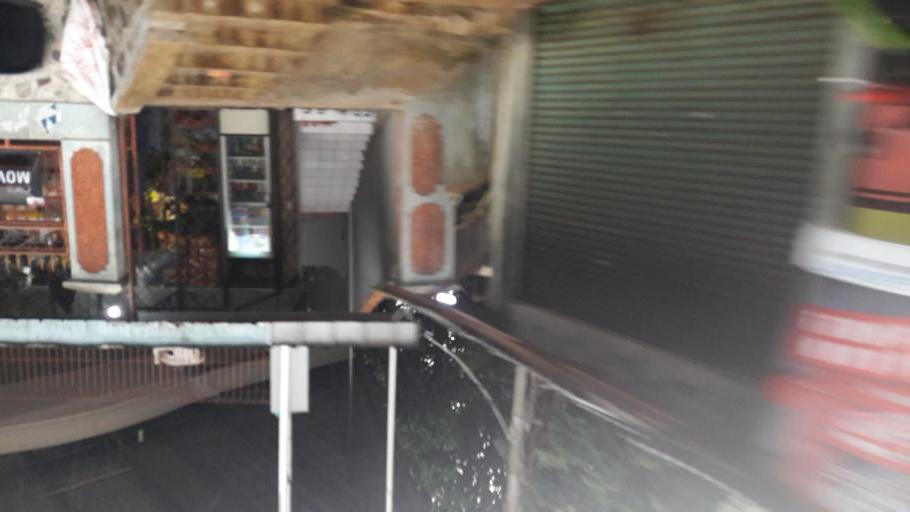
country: ID
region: West Java
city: Cipeundeuy
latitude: -6.6464
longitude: 106.5213
